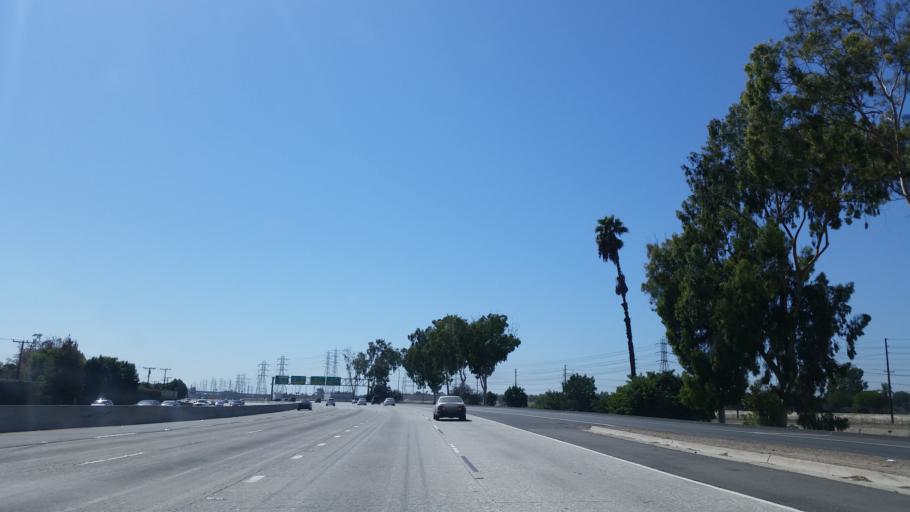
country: US
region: California
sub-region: Orange County
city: Los Alamitos
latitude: 33.7997
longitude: -118.0844
